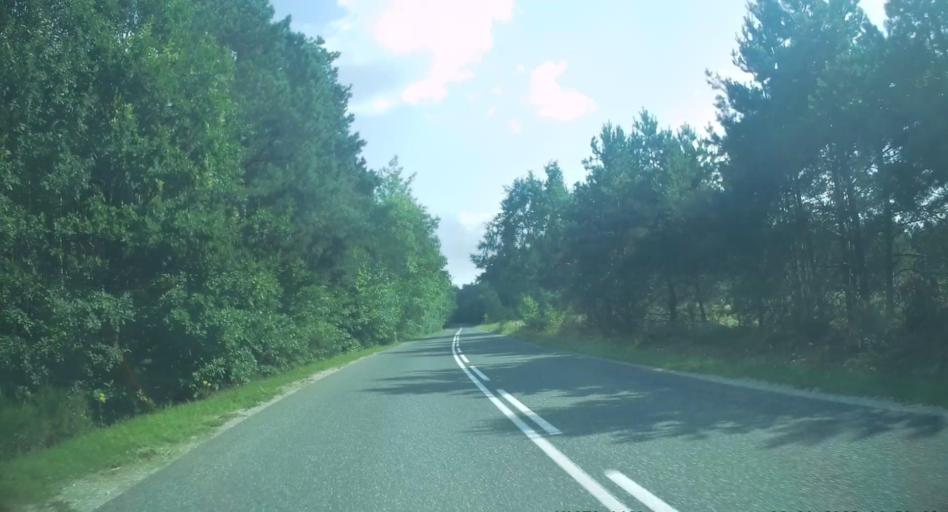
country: PL
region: Swietokrzyskie
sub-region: Powiat kielecki
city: Lopuszno
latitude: 50.8908
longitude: 20.2573
